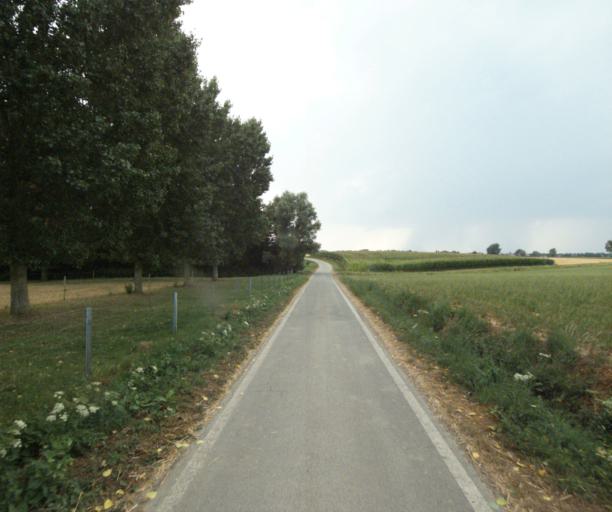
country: FR
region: Nord-Pas-de-Calais
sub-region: Departement du Nord
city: Deulemont
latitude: 50.7246
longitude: 2.9654
